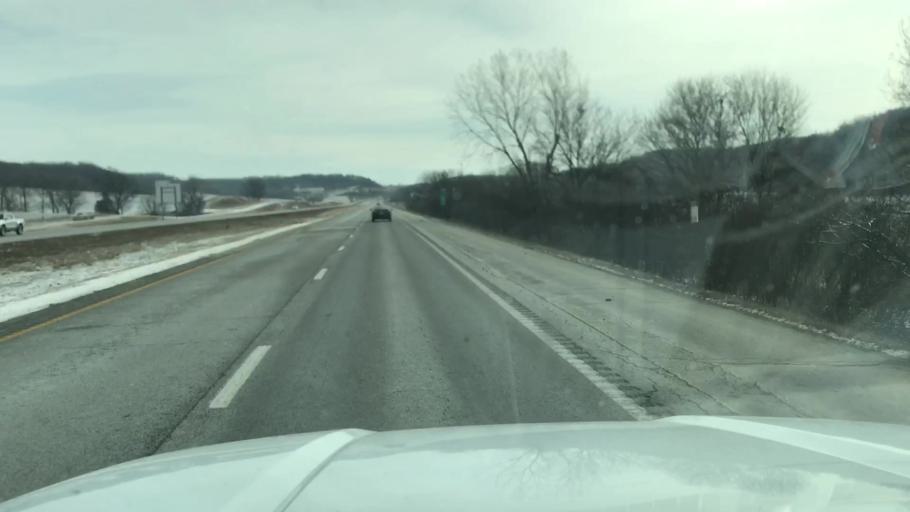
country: US
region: Missouri
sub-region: Holt County
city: Oregon
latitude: 39.9708
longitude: -94.9915
